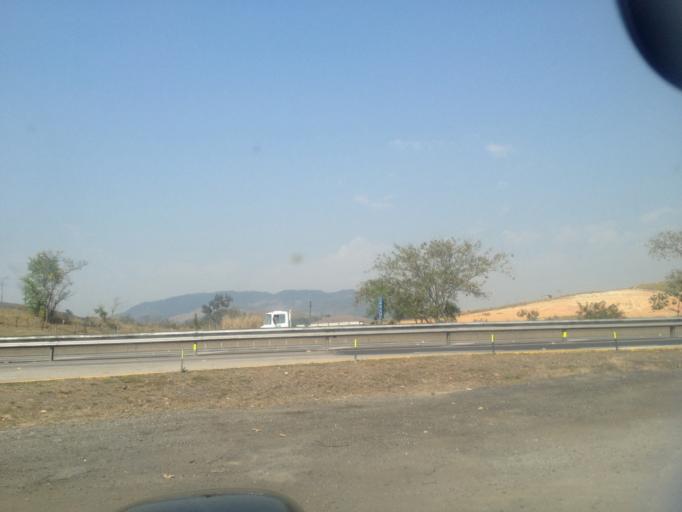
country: BR
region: Rio de Janeiro
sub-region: Porto Real
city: Porto Real
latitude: -22.4507
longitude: -44.3086
